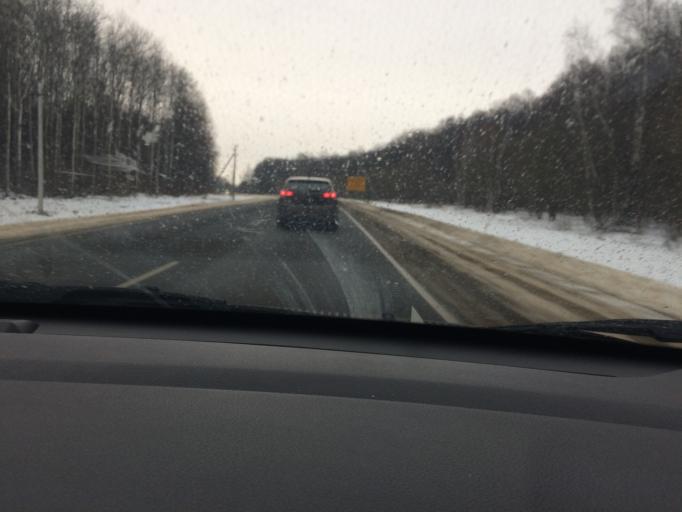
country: RU
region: Tula
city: Venev
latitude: 54.3358
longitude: 38.1301
